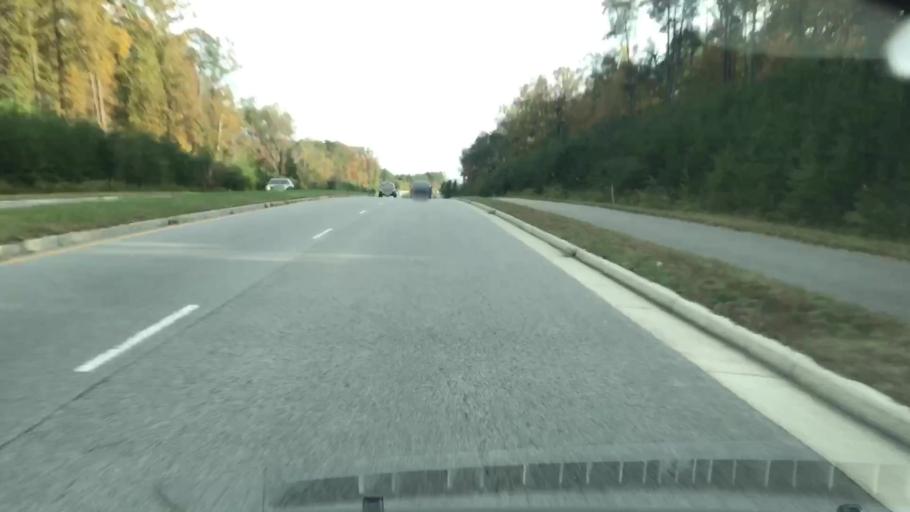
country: US
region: Virginia
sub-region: Fairfax County
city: Hayfield
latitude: 38.7359
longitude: -77.1467
